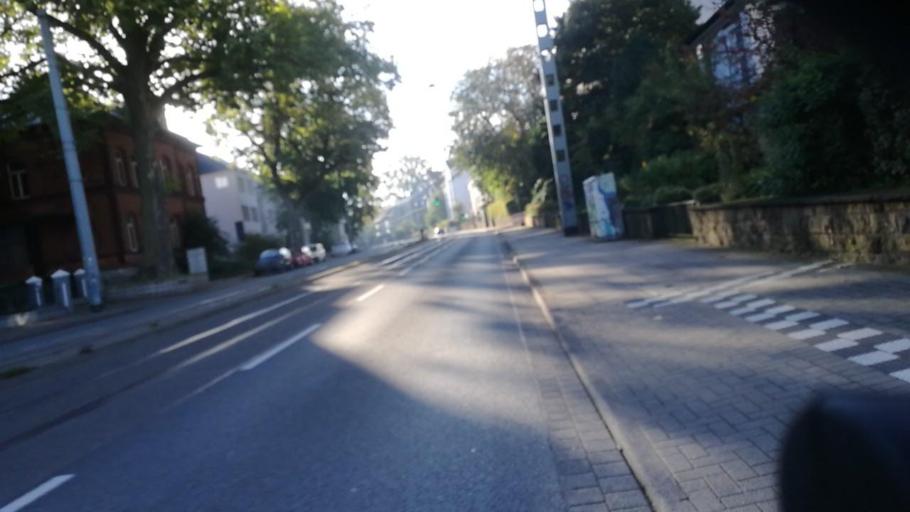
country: DE
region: North Rhine-Westphalia
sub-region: Regierungsbezirk Detmold
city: Bielefeld
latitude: 52.0147
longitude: 8.5331
